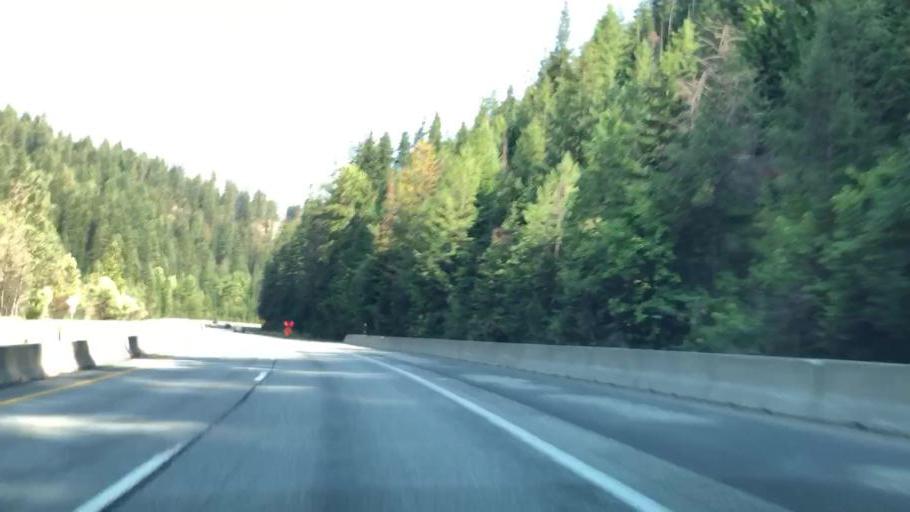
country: US
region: Idaho
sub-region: Shoshone County
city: Pinehurst
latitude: 47.5907
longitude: -116.4896
